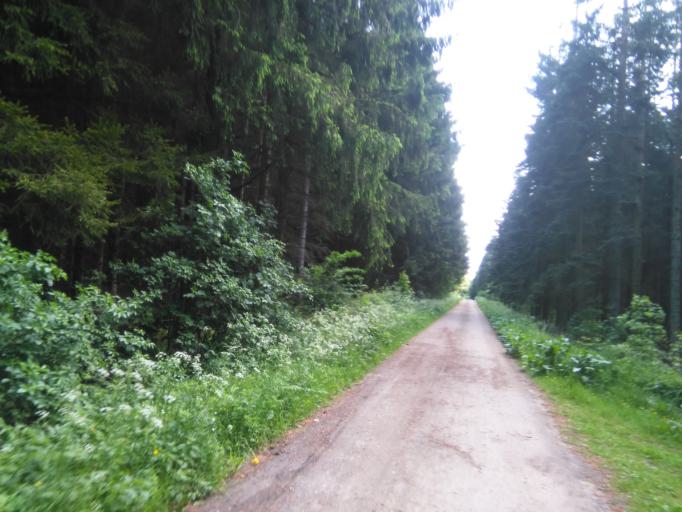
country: DK
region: Central Jutland
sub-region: Favrskov Kommune
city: Hinnerup
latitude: 56.2615
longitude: 10.0510
